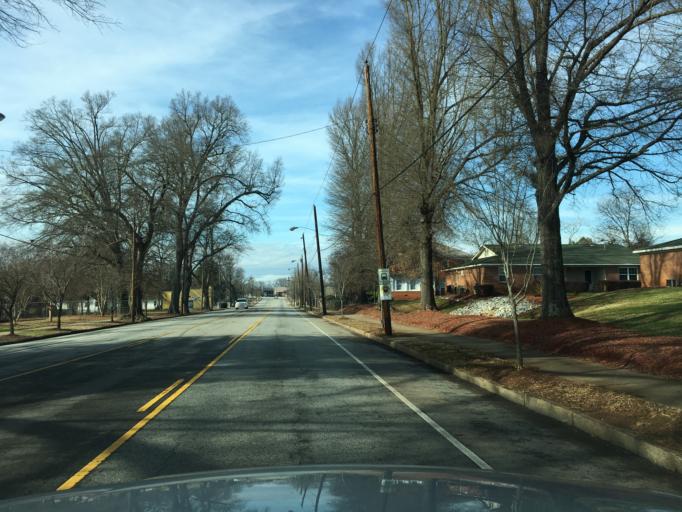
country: US
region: South Carolina
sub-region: Greenville County
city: Greenville
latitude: 34.8555
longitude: -82.4097
